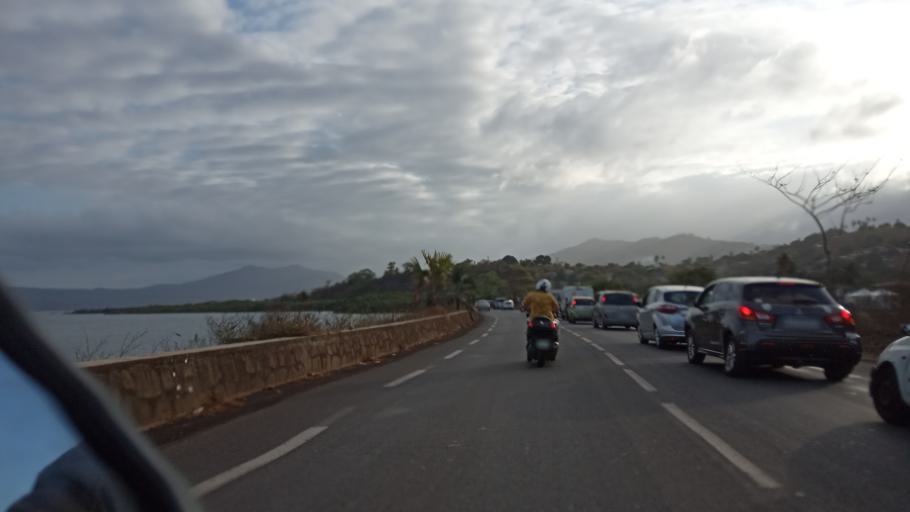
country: YT
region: Mamoudzou
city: Mamoudzou
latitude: -12.7934
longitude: 45.2194
